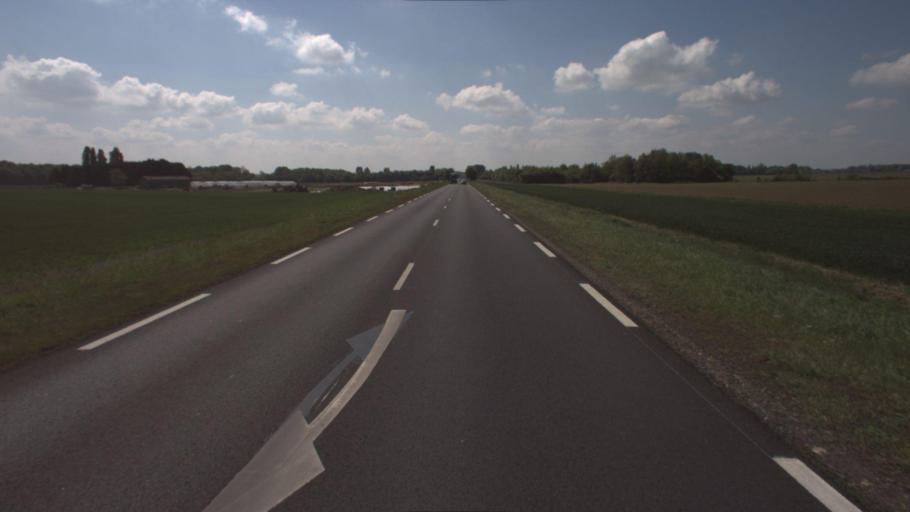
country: FR
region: Ile-de-France
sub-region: Departement de Seine-et-Marne
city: La Houssaye-en-Brie
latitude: 48.7560
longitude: 2.8589
